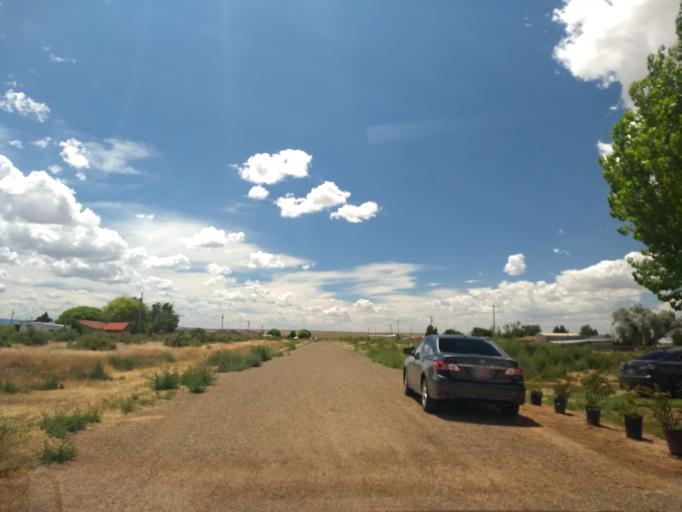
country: US
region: Arizona
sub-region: Coconino County
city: Fredonia
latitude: 36.9440
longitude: -112.5193
